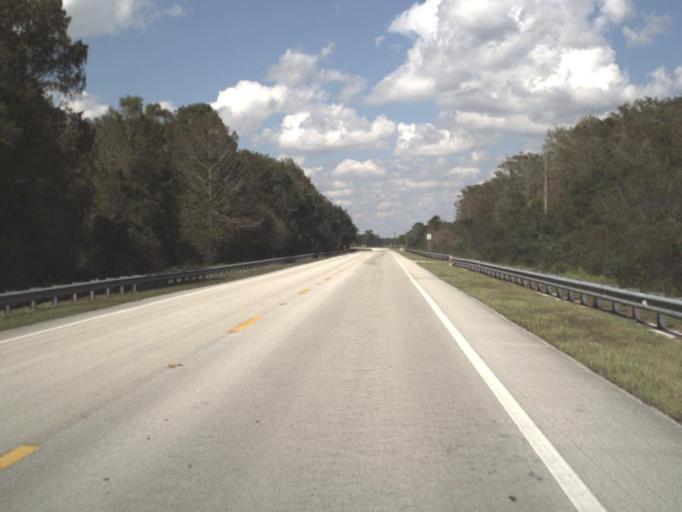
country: US
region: Florida
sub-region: Okeechobee County
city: Okeechobee
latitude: 27.3798
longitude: -80.9893
